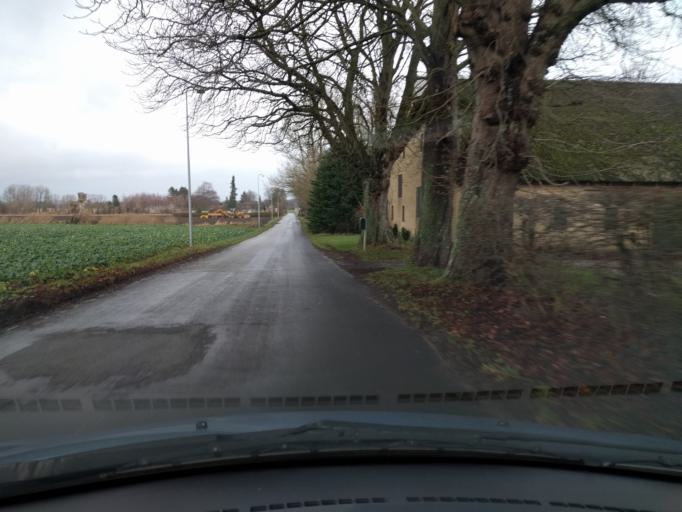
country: DK
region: South Denmark
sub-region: Kerteminde Kommune
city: Langeskov
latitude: 55.3407
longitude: 10.5430
